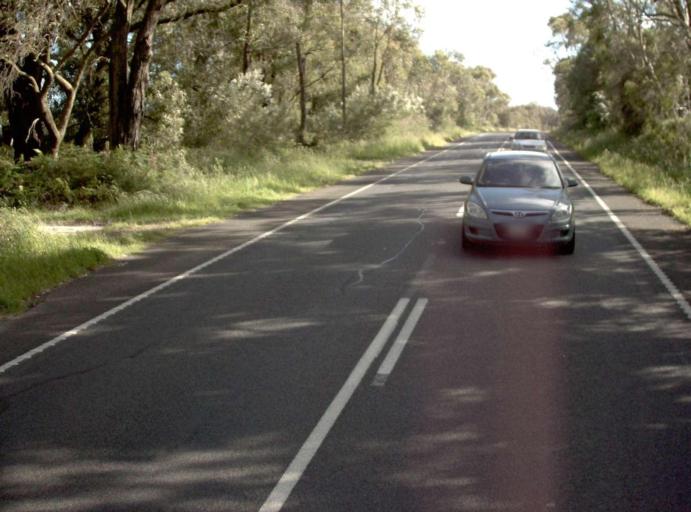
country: AU
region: Victoria
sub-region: Bass Coast
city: North Wonthaggi
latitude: -38.5596
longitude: 145.8426
